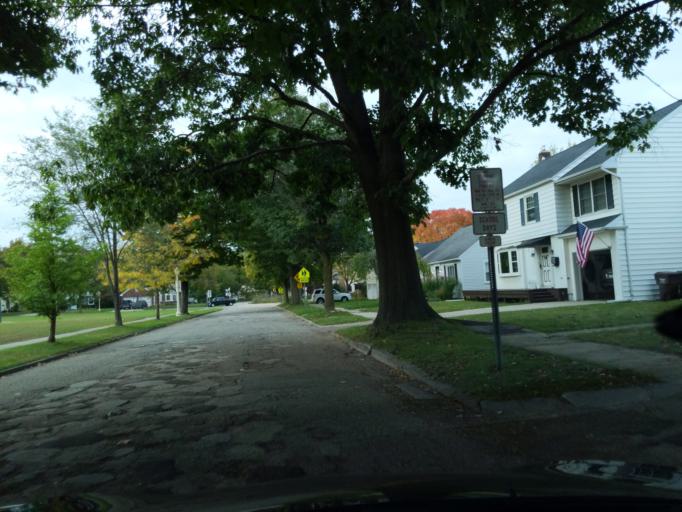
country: US
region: Michigan
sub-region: Ingham County
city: Lansing
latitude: 42.7126
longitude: -84.5339
